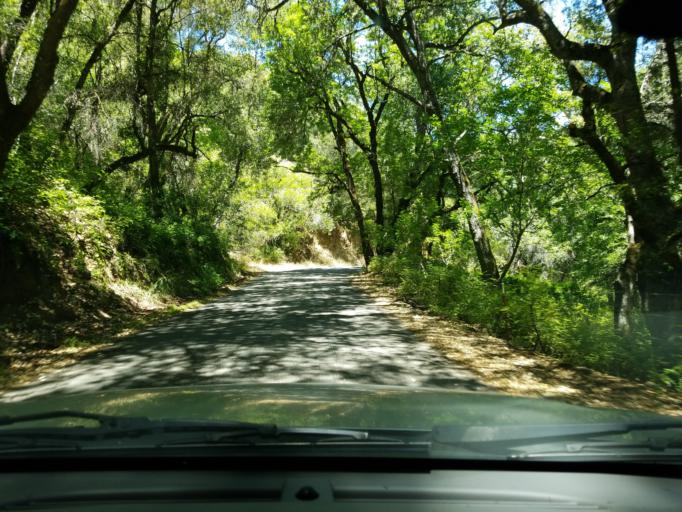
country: US
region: California
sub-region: Monterey County
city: Gonzales
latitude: 36.3600
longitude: -121.5515
